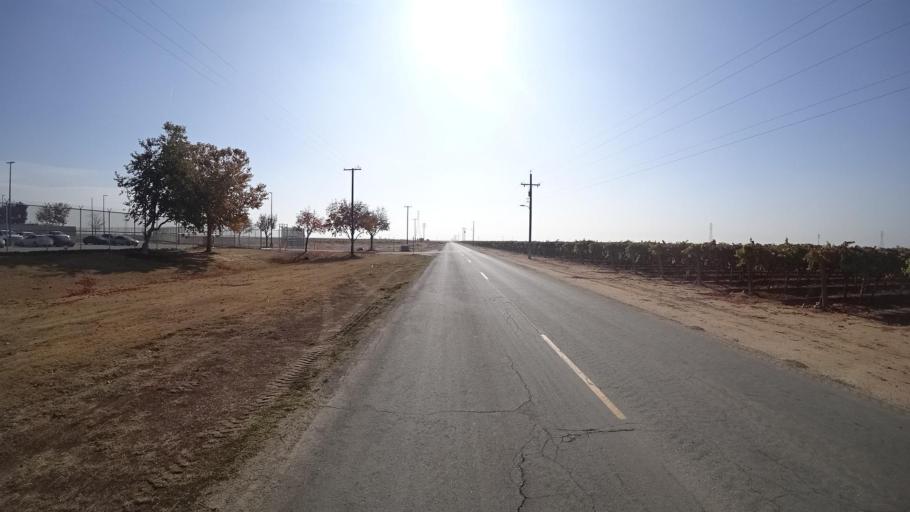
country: US
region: California
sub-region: Kern County
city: Greenacres
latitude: 35.5050
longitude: -119.1167
